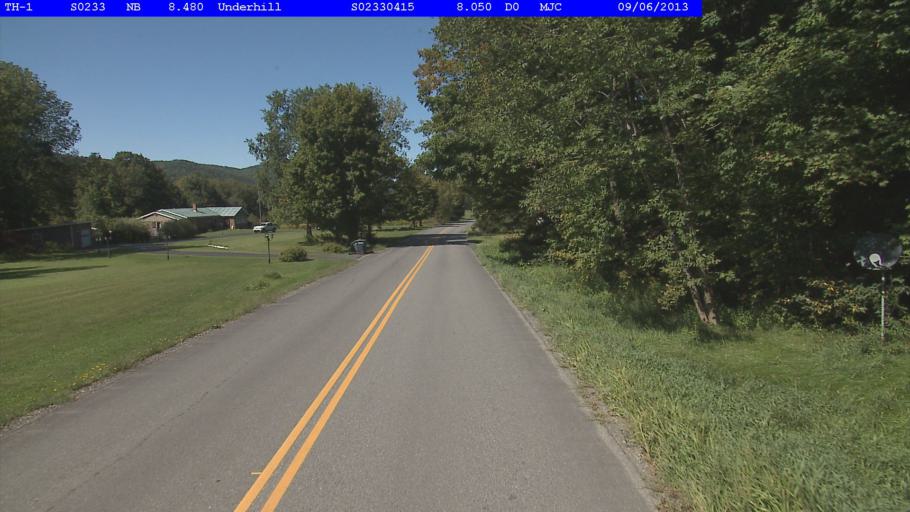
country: US
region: Vermont
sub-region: Chittenden County
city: Jericho
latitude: 44.5805
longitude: -72.8629
